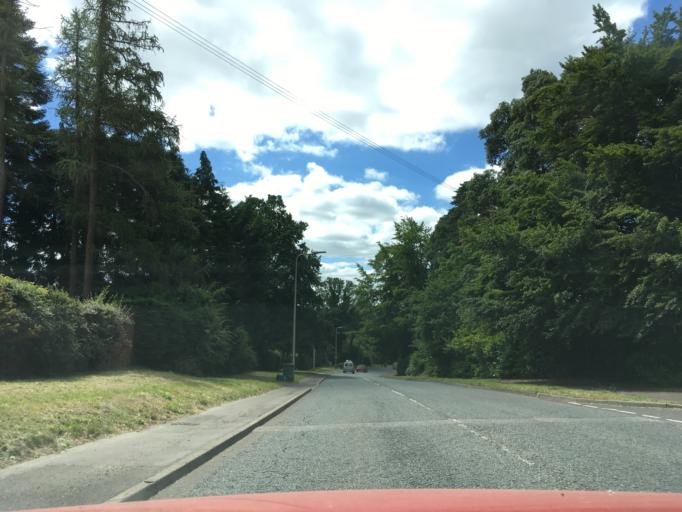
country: GB
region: England
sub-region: West Berkshire
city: Newbury
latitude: 51.3724
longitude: -1.3466
